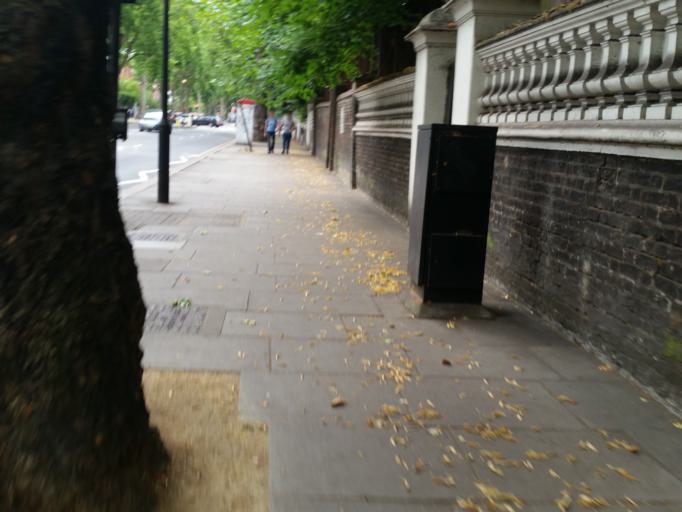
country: GB
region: England
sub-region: Greater London
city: Kensington
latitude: 51.5071
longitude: -0.2056
